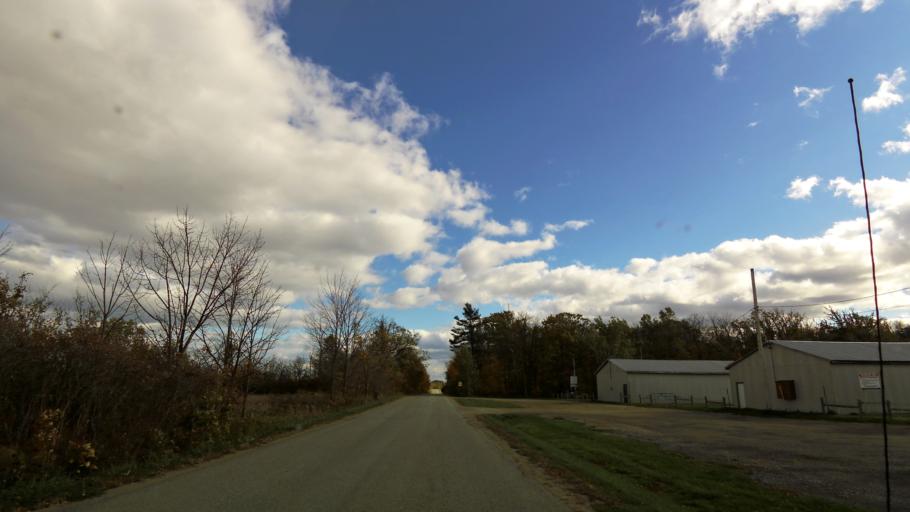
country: CA
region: Ontario
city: Burlington
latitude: 43.4462
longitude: -79.8512
